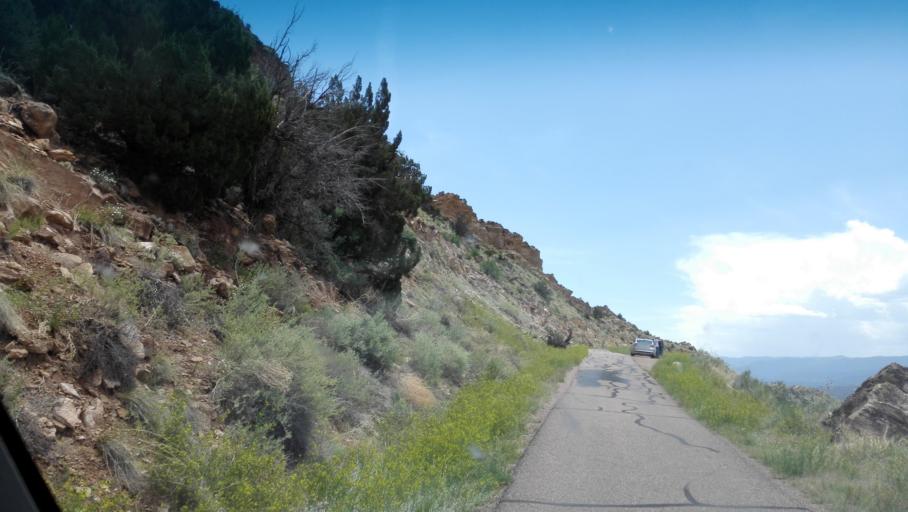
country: US
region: Colorado
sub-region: Fremont County
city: Canon City
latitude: 38.4683
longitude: -105.2545
